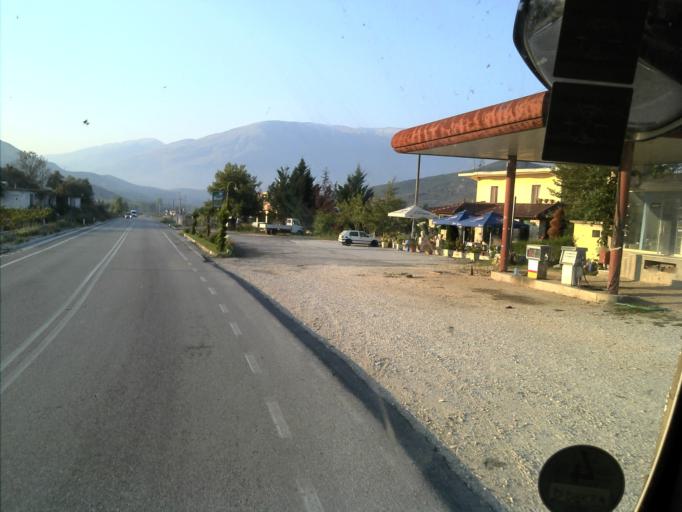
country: AL
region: Gjirokaster
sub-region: Rrethi i Tepelenes
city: Krahes
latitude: 40.4285
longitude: 19.8530
